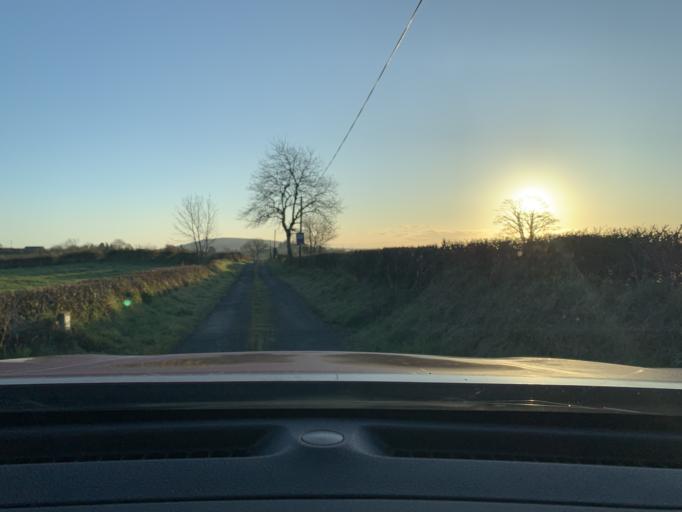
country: IE
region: Connaught
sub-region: Sligo
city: Ballymote
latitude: 54.0668
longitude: -8.5520
